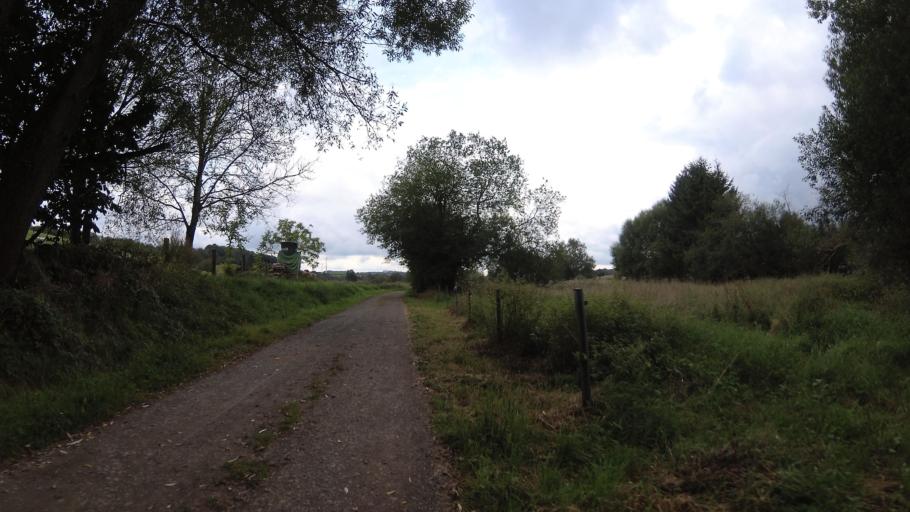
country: DE
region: Rheinland-Pfalz
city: Reichweiler
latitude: 49.5230
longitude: 7.2708
